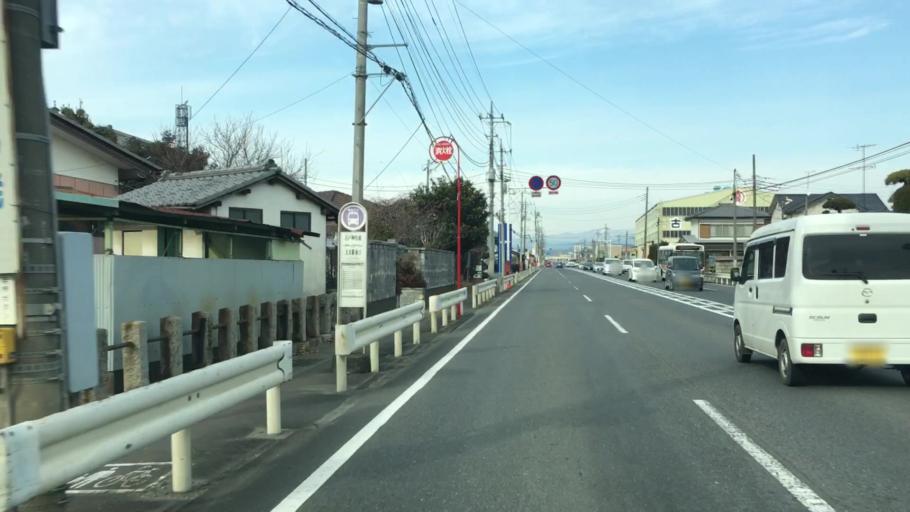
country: JP
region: Saitama
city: Menuma
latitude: 36.2498
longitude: 139.3790
